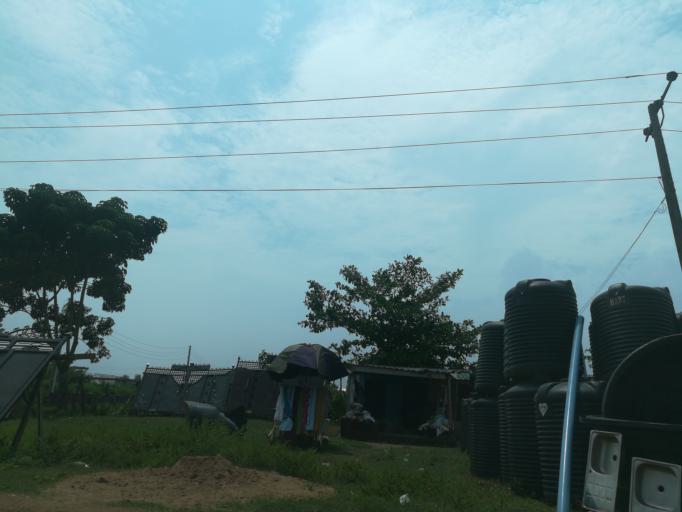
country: NG
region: Lagos
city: Ikorodu
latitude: 6.5938
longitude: 3.6246
